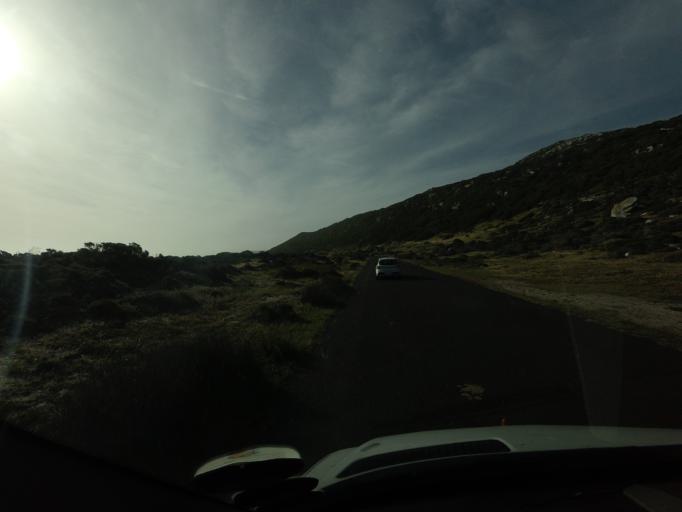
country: ZA
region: Western Cape
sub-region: City of Cape Town
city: Retreat
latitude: -34.3484
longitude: 18.4679
